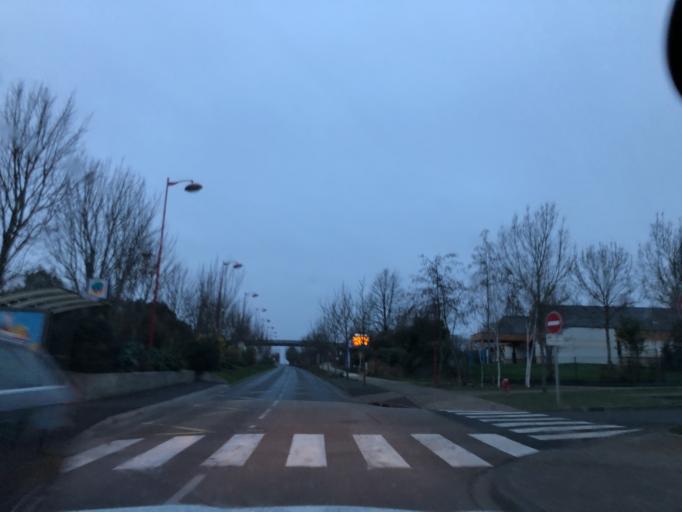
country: FR
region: Lower Normandy
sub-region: Departement du Calvados
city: Blainville-sur-Orne
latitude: 49.2301
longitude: -0.3023
